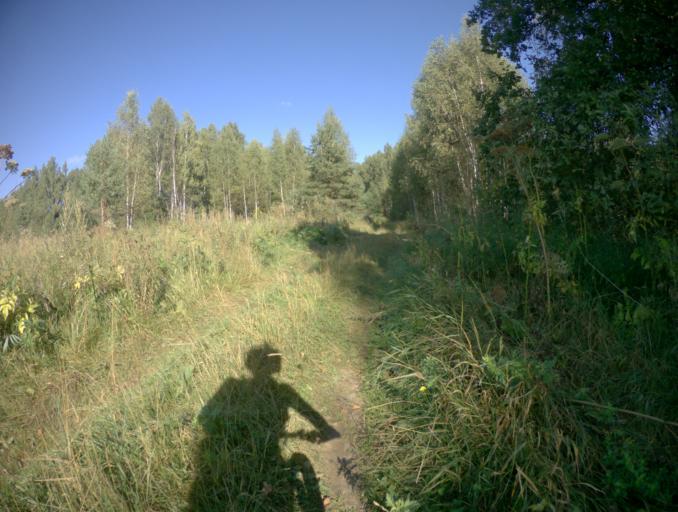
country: RU
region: Vladimir
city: Sudogda
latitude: 56.1276
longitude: 40.7936
